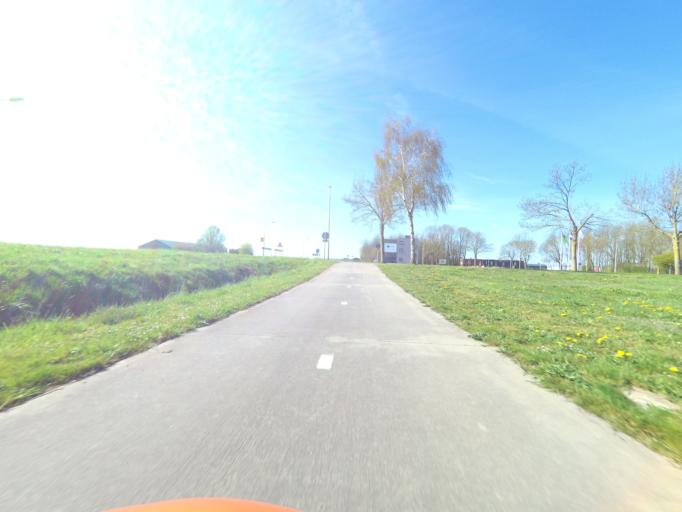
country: NL
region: Flevoland
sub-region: Gemeente Lelystad
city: Lelystad
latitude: 52.4543
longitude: 5.5282
